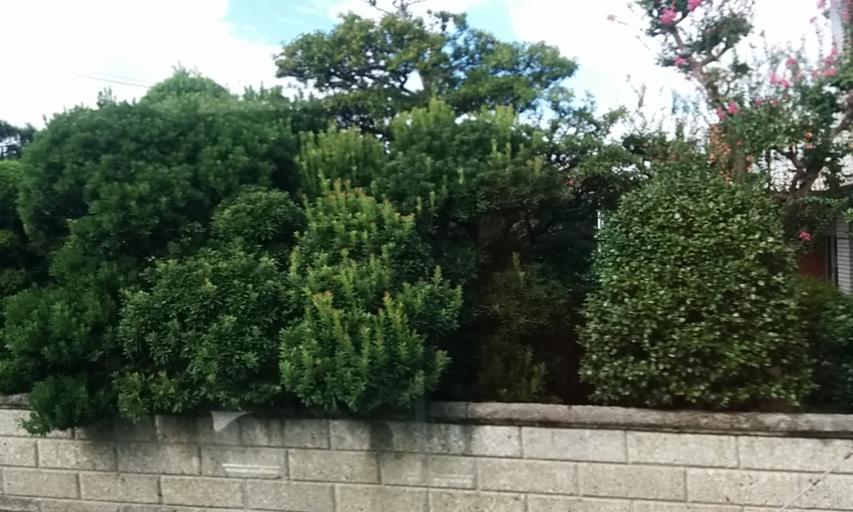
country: JP
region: Nara
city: Kashihara-shi
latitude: 34.5300
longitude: 135.7945
